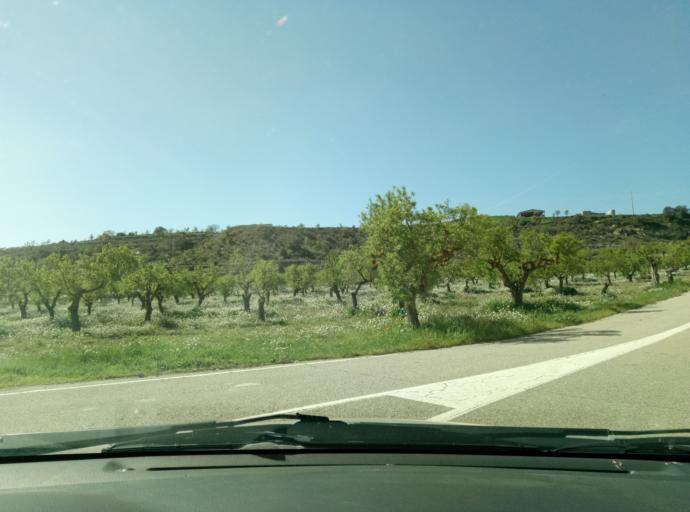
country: ES
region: Catalonia
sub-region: Provincia de Lleida
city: Vallbona de les Monges
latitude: 41.5509
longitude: 1.0311
